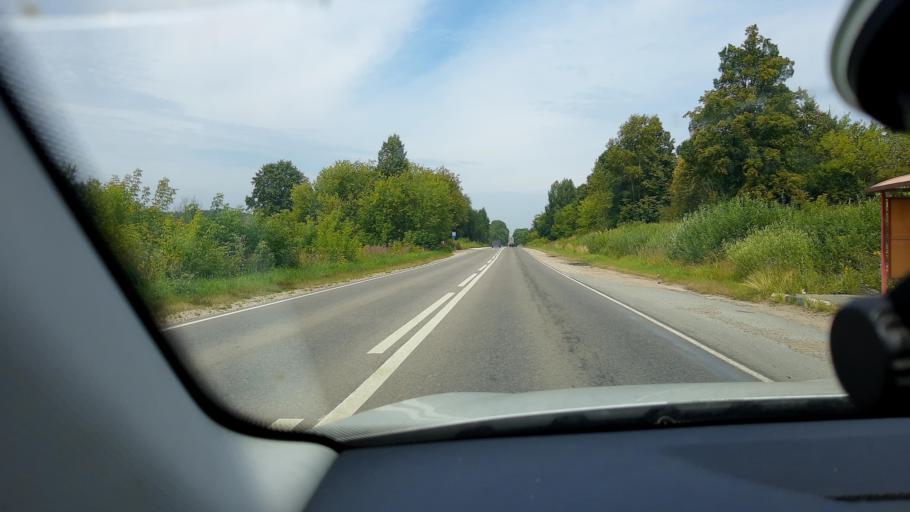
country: RU
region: Tula
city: Zaokskiy
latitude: 54.7734
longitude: 37.4356
